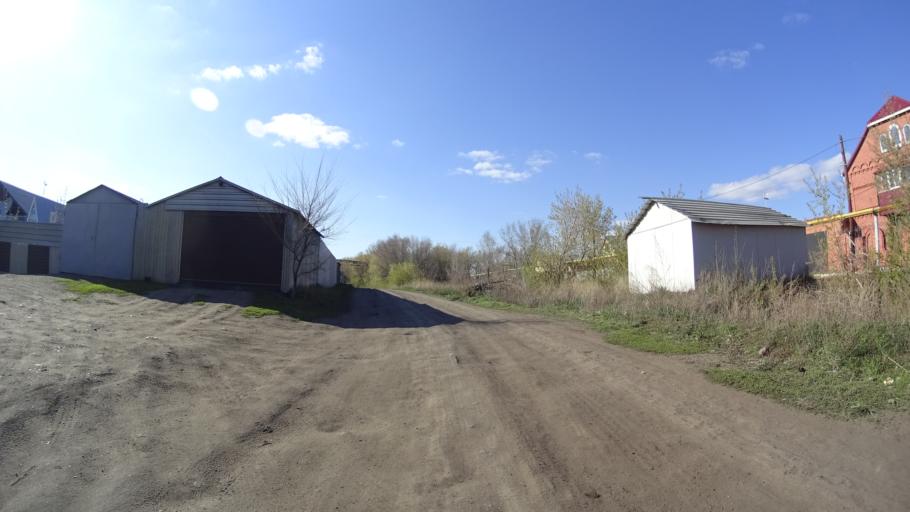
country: RU
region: Chelyabinsk
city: Troitsk
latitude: 54.1061
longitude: 61.5592
